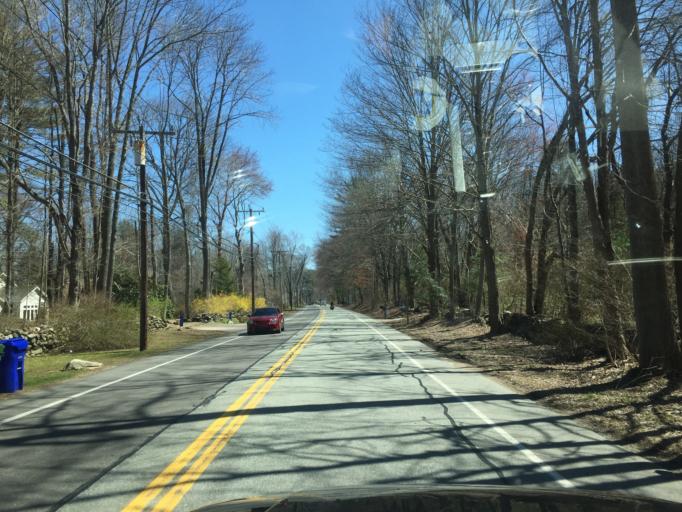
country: US
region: Connecticut
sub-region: Hartford County
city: Terramuggus
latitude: 41.6393
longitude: -72.4733
